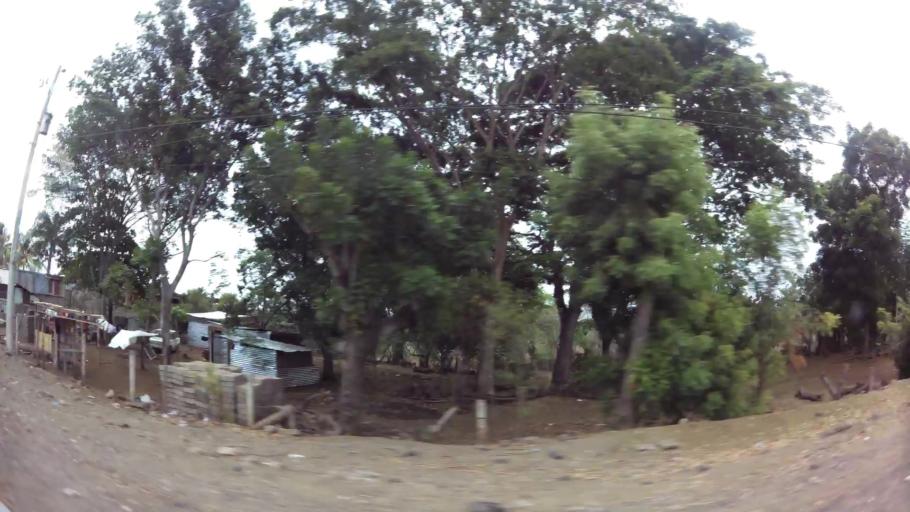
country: NI
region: Masaya
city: Ticuantepe
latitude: 12.0872
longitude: -86.1873
